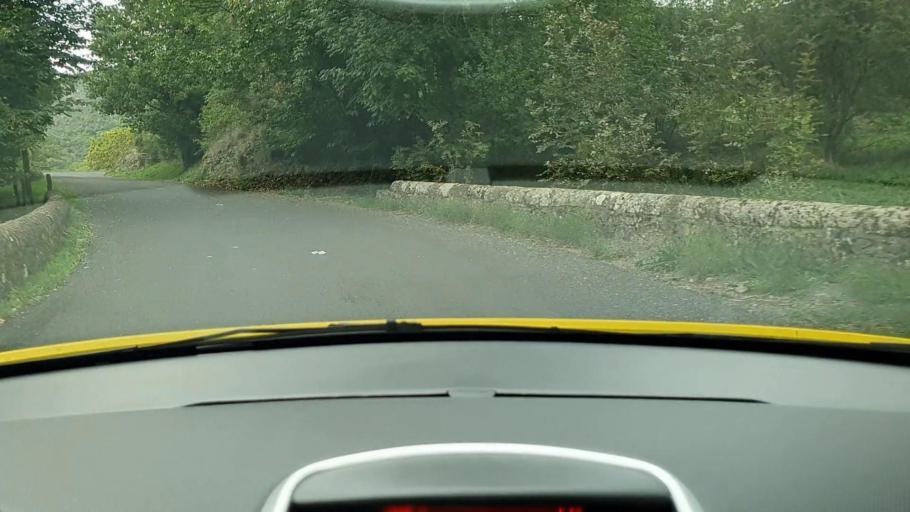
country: FR
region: Languedoc-Roussillon
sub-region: Departement de la Lozere
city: Meyrueis
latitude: 44.0670
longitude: 3.4417
